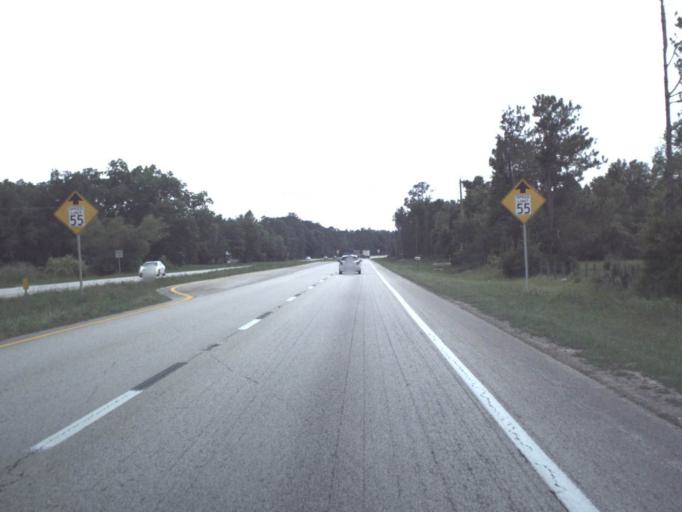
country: US
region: Florida
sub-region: Bradford County
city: Starke
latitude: 30.0661
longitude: -82.0662
